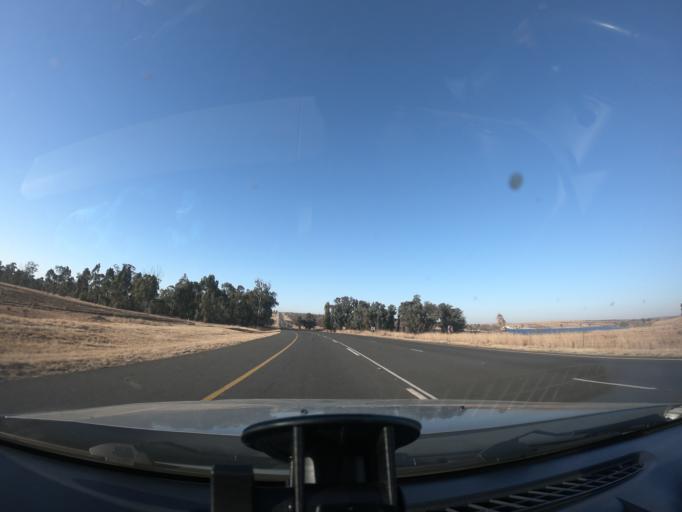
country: ZA
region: Mpumalanga
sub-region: Gert Sibande District Municipality
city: Ermelo
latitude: -26.4603
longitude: 29.9520
